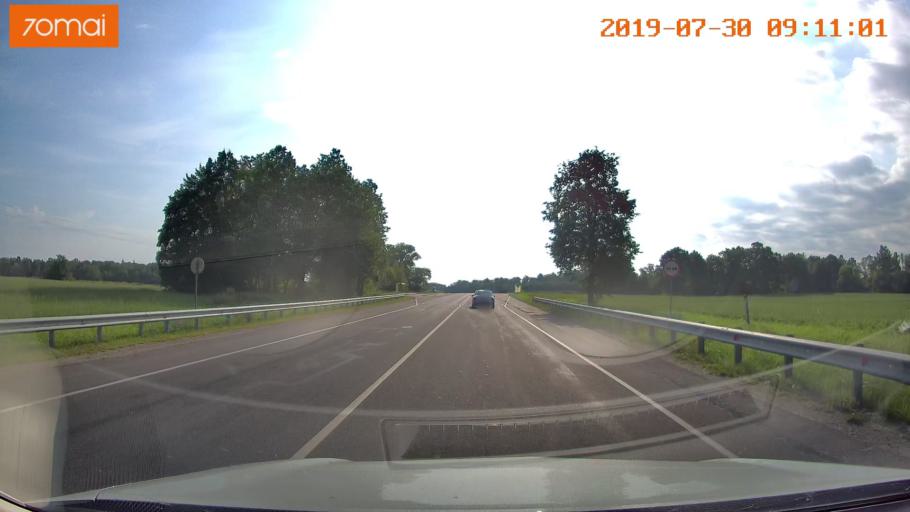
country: RU
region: Kaliningrad
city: Nesterov
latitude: 54.6117
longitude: 22.4419
